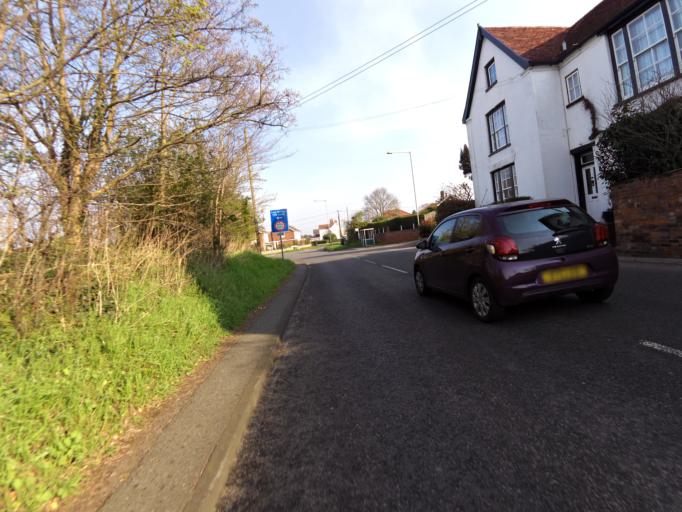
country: GB
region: England
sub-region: Suffolk
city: Bramford
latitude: 52.0759
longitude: 1.1068
